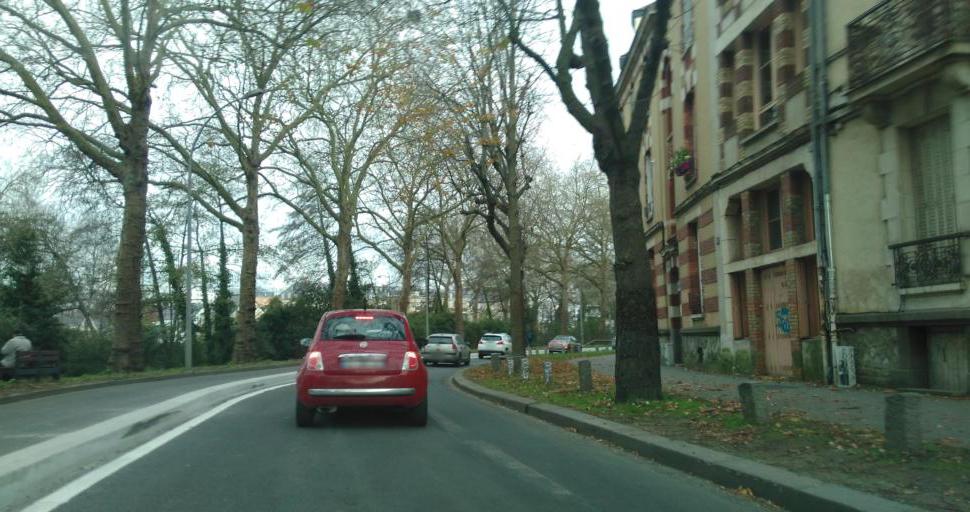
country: FR
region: Brittany
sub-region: Departement d'Ille-et-Vilaine
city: Rennes
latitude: 48.1141
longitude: -1.6874
